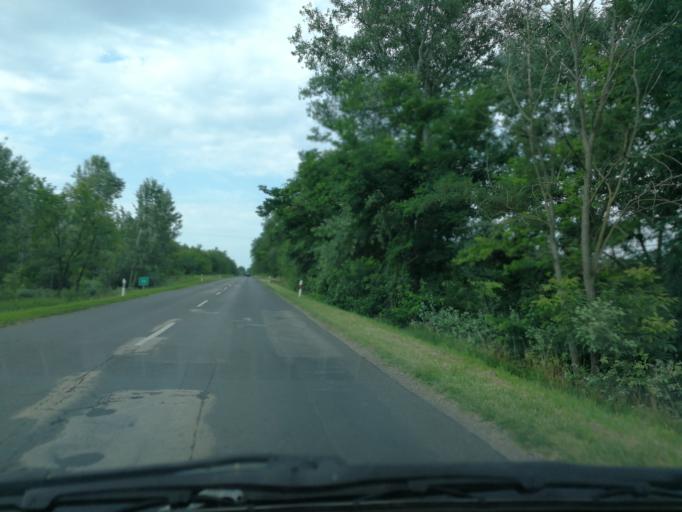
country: HU
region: Bacs-Kiskun
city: Ersekcsanad
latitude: 46.2311
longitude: 18.9725
